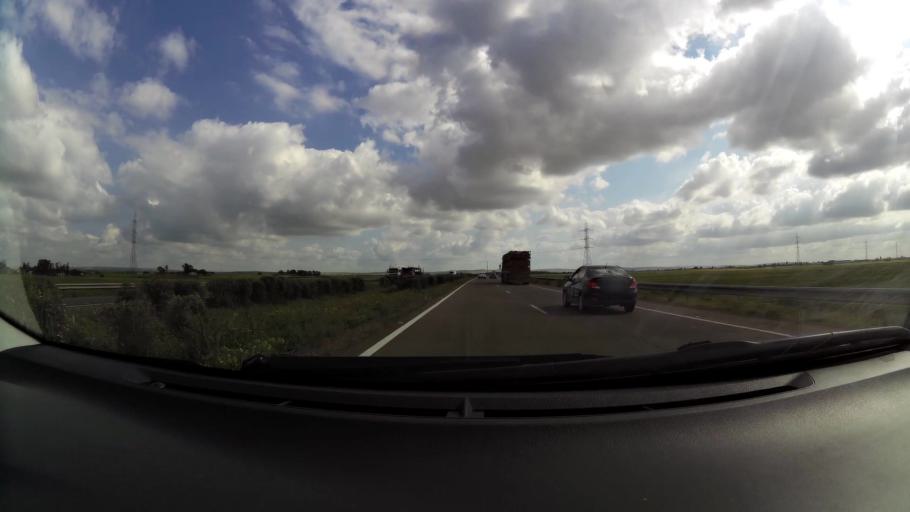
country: MA
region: Chaouia-Ouardigha
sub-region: Settat Province
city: Berrechid
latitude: 33.1570
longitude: -7.5709
